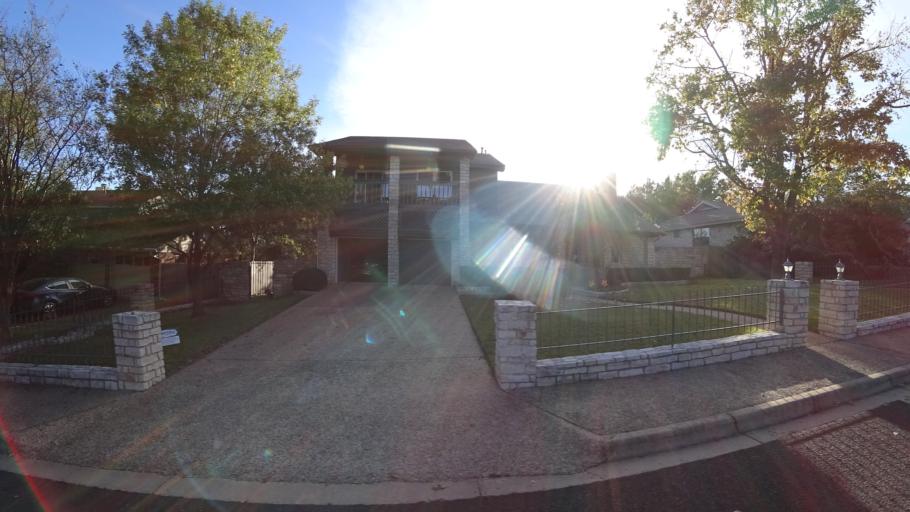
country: US
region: Texas
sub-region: Williamson County
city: Jollyville
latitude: 30.4076
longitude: -97.7570
